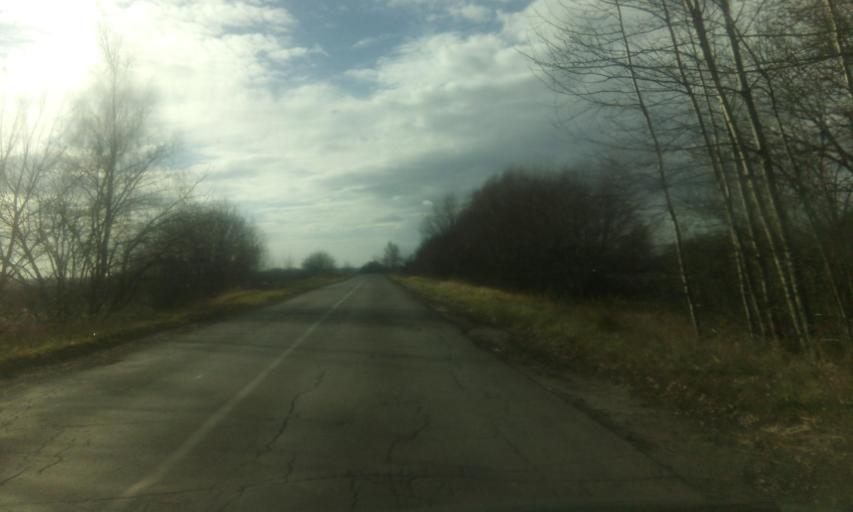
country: RU
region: Tula
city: Dubovka
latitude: 53.9574
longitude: 38.0403
